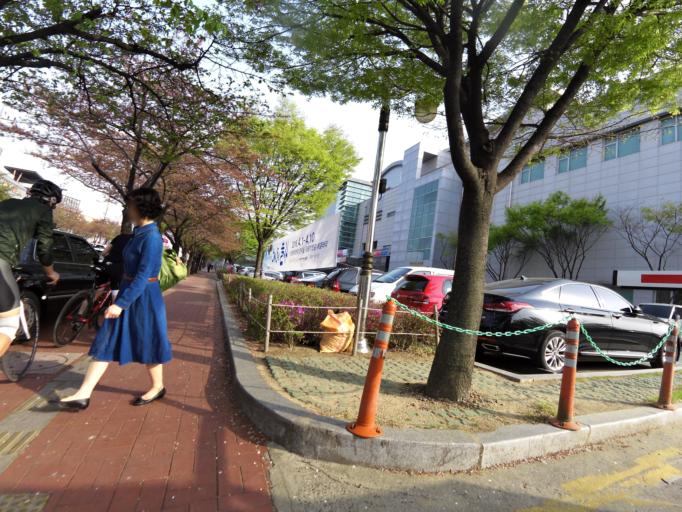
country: KR
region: Daegu
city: Daegu
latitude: 35.8803
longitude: 128.6518
